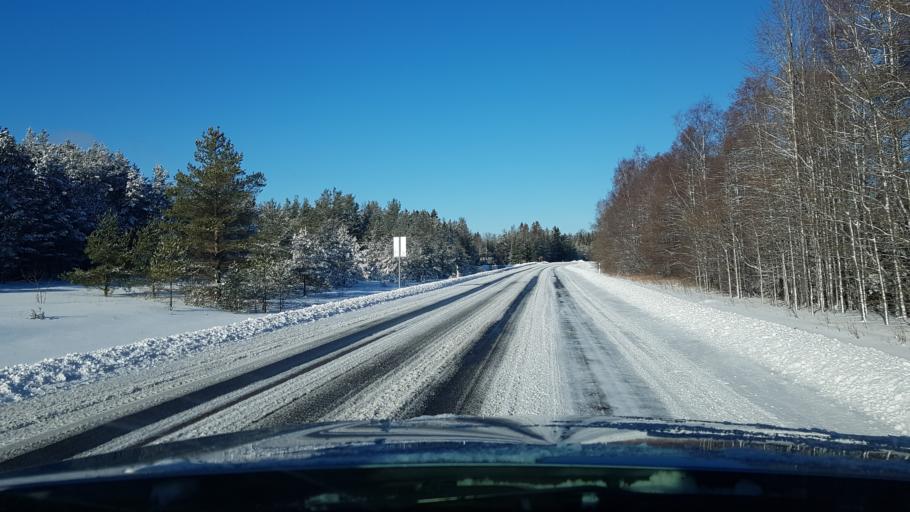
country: EE
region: Hiiumaa
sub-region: Kaerdla linn
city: Kardla
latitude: 58.9599
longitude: 22.7727
